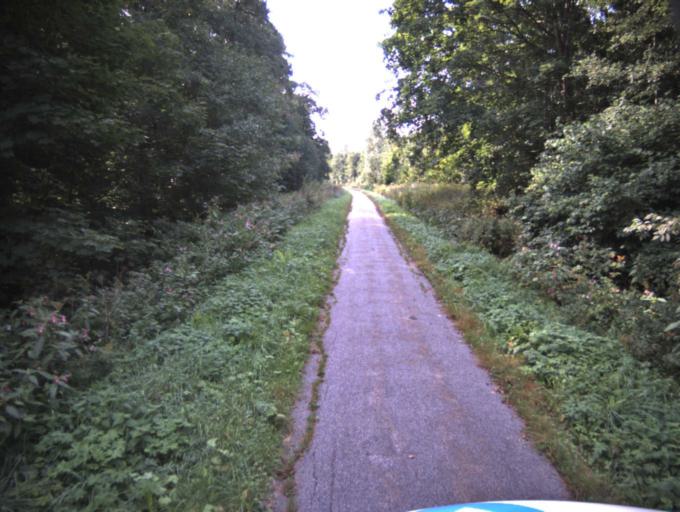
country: SE
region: Vaestra Goetaland
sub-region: Tranemo Kommun
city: Limmared
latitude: 57.6627
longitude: 13.3635
